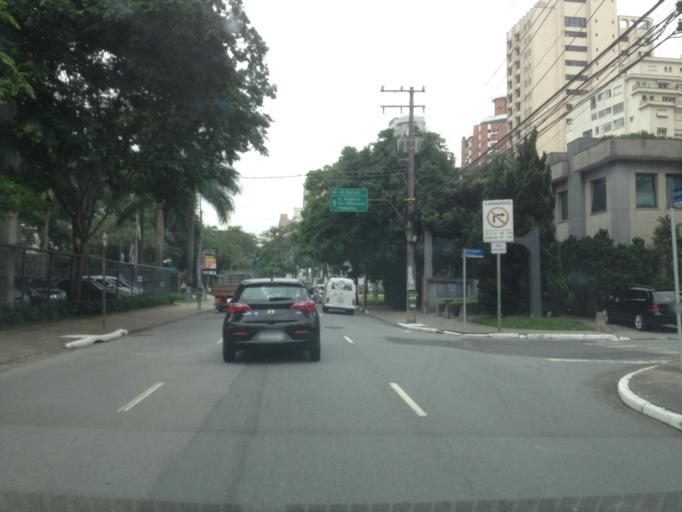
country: BR
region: Sao Paulo
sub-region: Sao Paulo
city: Sao Paulo
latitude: -23.5709
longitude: -46.6638
